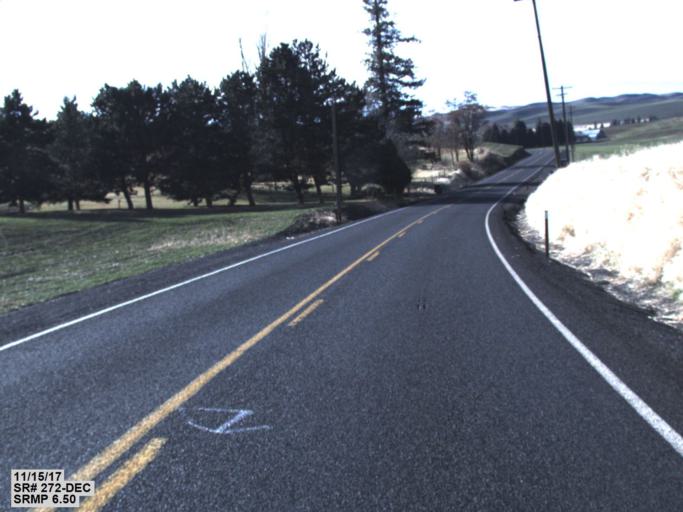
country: US
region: Washington
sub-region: Whitman County
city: Colfax
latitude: 46.9225
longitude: -117.2533
